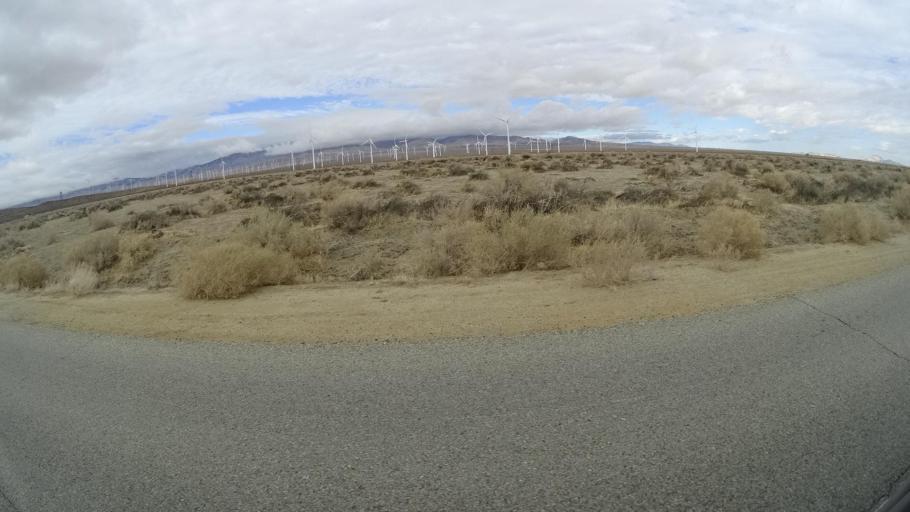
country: US
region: California
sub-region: Los Angeles County
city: Green Valley
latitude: 34.8626
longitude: -118.4168
